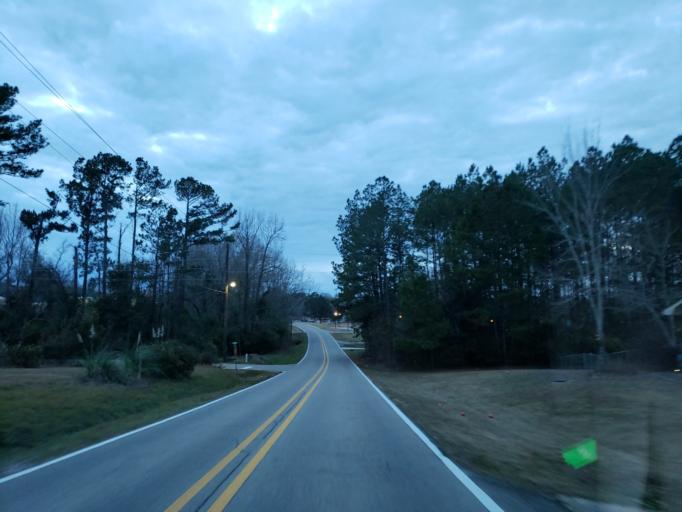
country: US
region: Mississippi
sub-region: Forrest County
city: Petal
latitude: 31.3428
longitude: -89.2481
